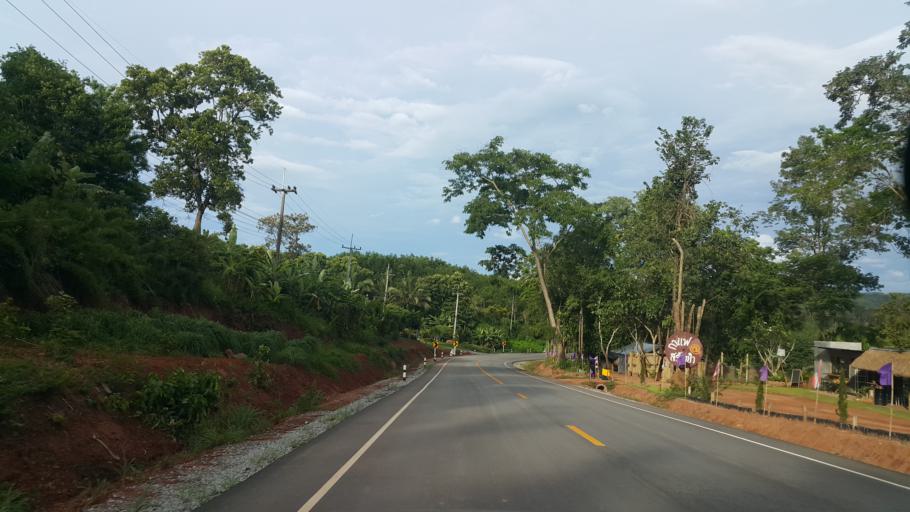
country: TH
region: Loei
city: Na Haeo
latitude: 17.4996
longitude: 101.0500
